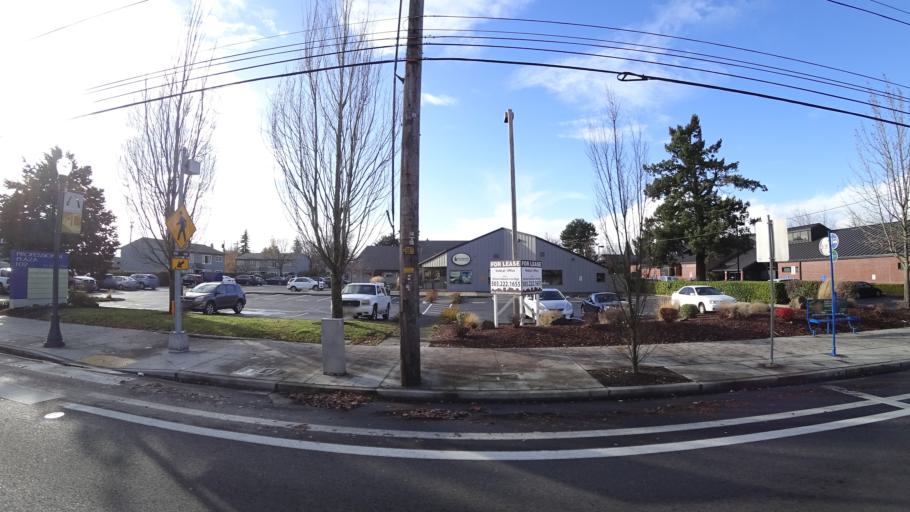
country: US
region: Oregon
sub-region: Multnomah County
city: Lents
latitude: 45.5241
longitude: -122.5583
